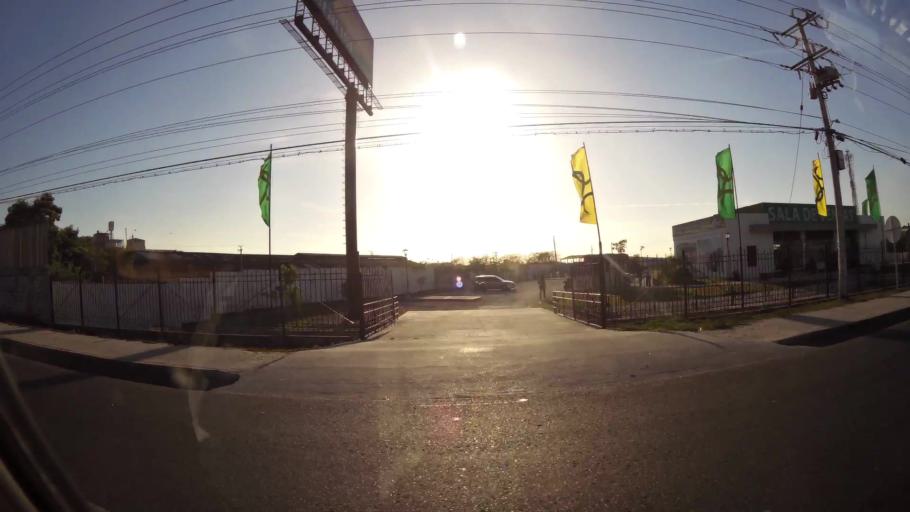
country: CO
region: Atlantico
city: Soledad
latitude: 10.9194
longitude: -74.7758
